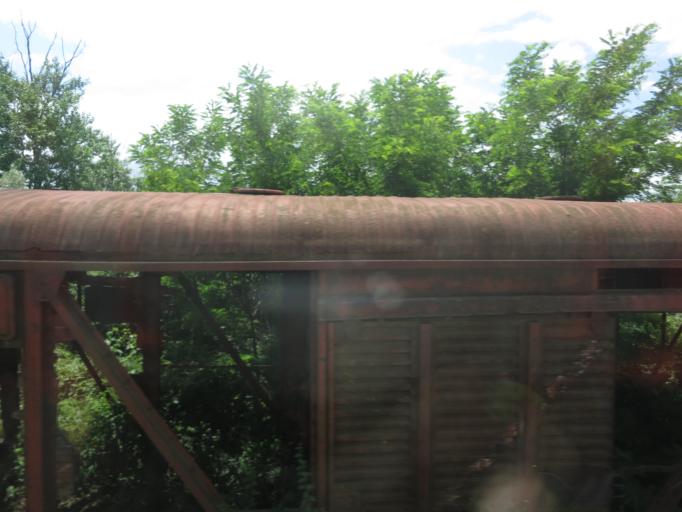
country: GE
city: Agara
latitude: 42.0248
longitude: 43.7500
